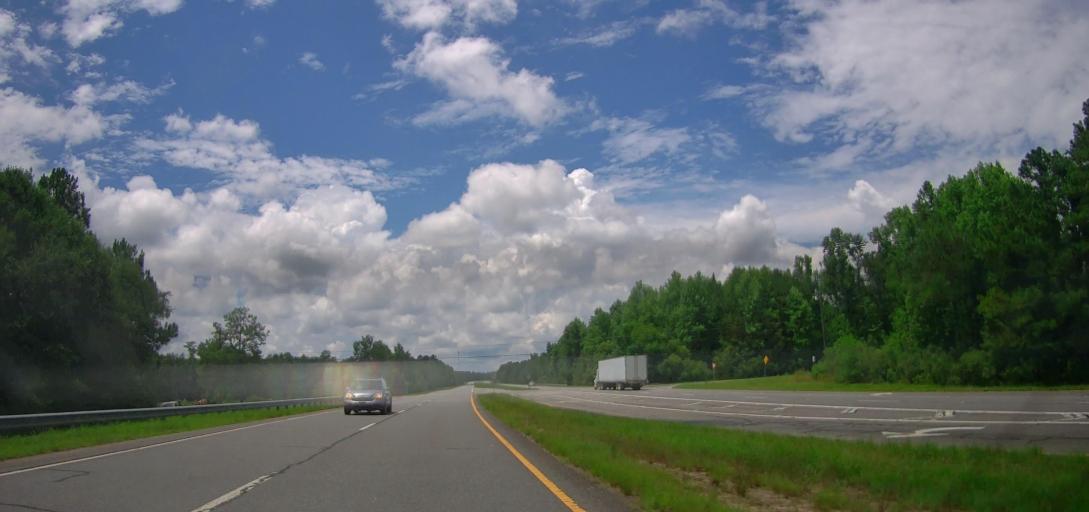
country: US
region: Georgia
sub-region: Dodge County
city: Eastman
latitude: 32.1799
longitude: -83.1912
